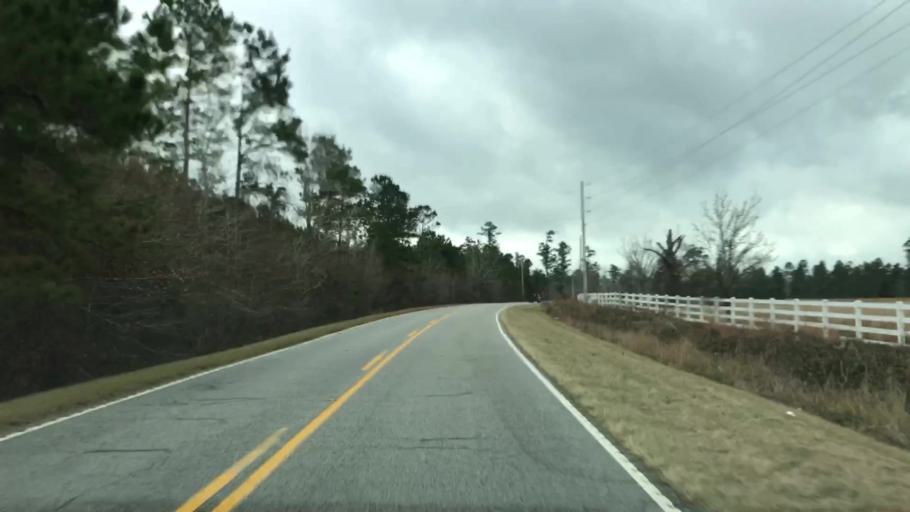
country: US
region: South Carolina
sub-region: Florence County
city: Johnsonville
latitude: 33.6505
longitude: -79.4195
